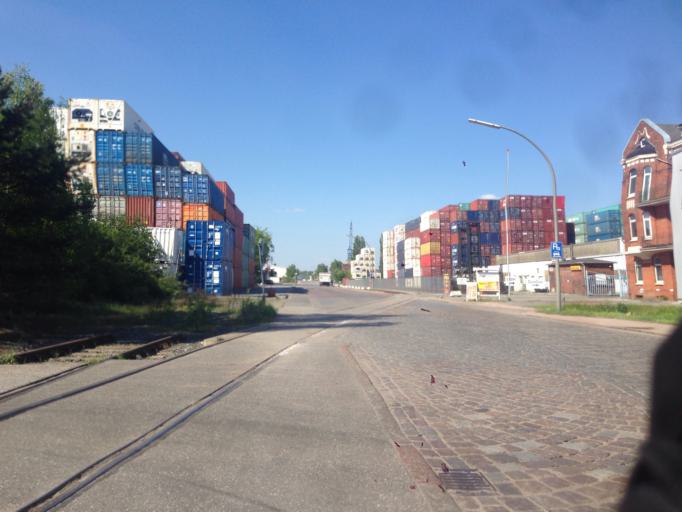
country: DE
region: Hamburg
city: Kleiner Grasbrook
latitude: 53.5302
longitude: 9.9734
